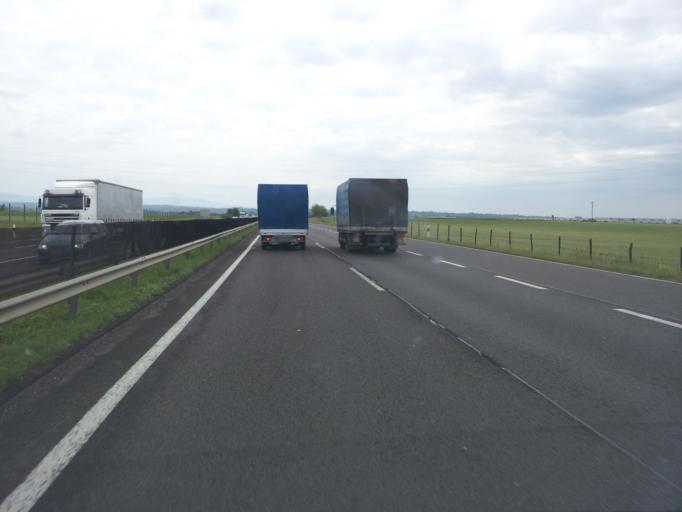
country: HU
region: Heves
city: Hered
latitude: 47.6699
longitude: 19.6301
